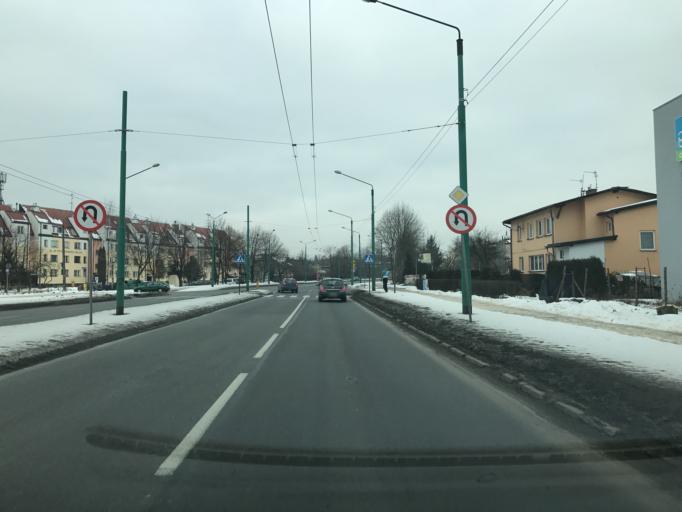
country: PL
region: Silesian Voivodeship
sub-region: Tychy
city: Cielmice
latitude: 50.1009
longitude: 19.0013
